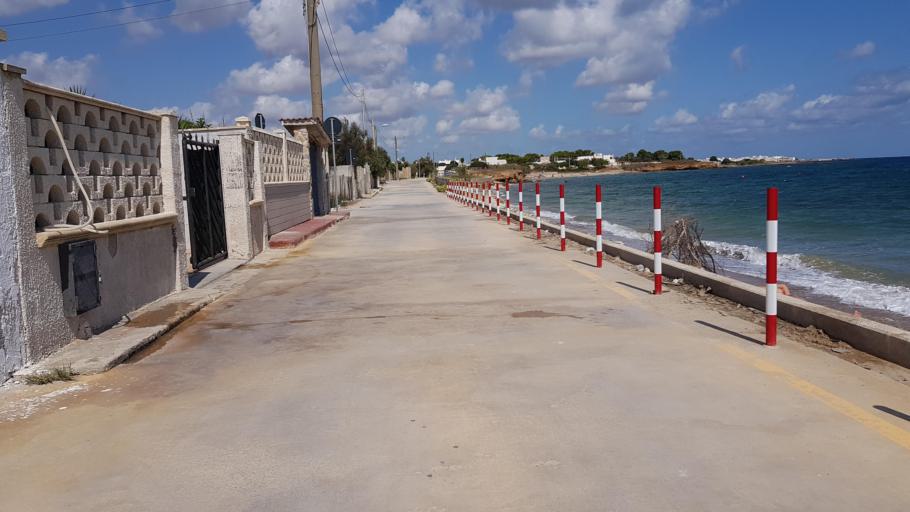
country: IT
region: Apulia
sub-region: Provincia di Brindisi
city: Torchiarolo
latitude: 40.5247
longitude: 18.0814
